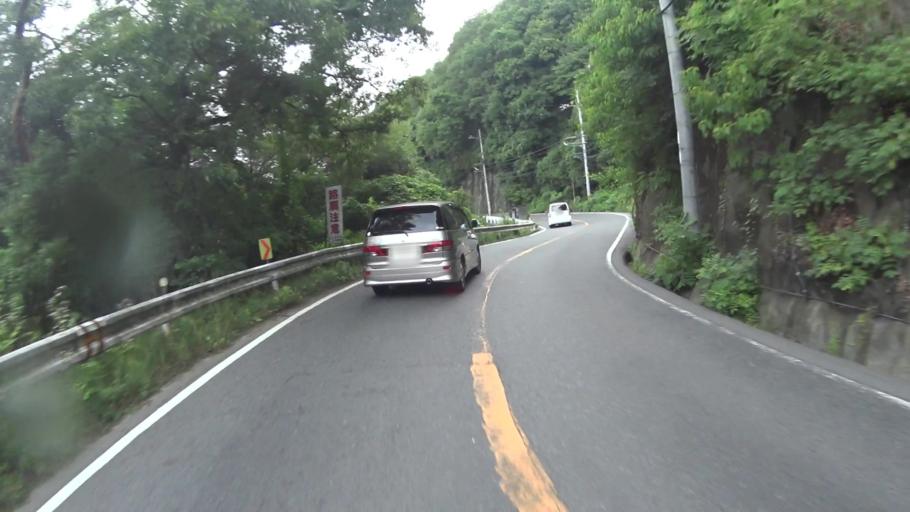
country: JP
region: Kyoto
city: Uji
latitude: 34.8570
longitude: 135.8998
